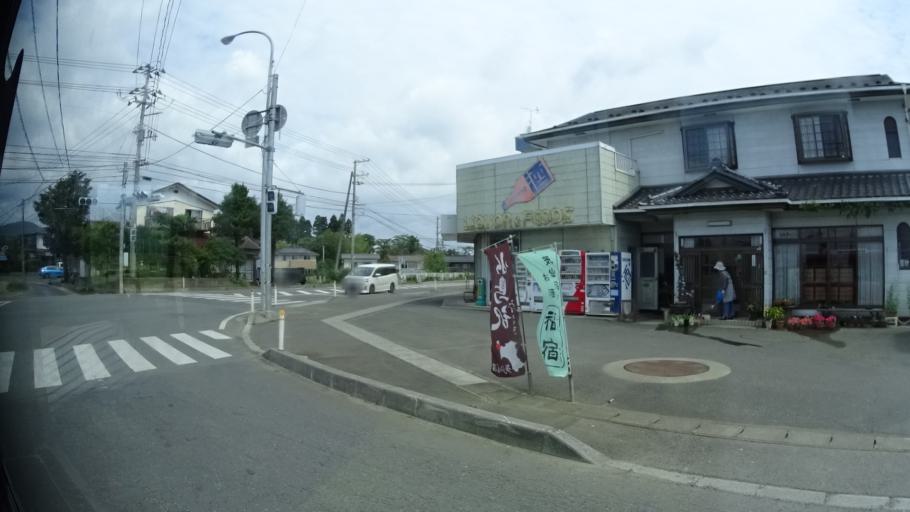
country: JP
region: Iwate
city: Ofunato
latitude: 38.8354
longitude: 141.5788
